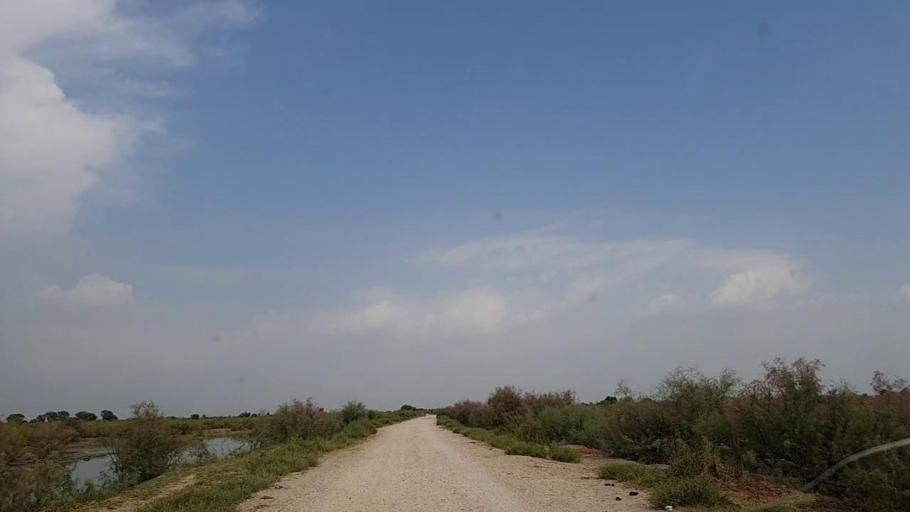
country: PK
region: Sindh
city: Khanpur
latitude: 27.8291
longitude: 69.5110
